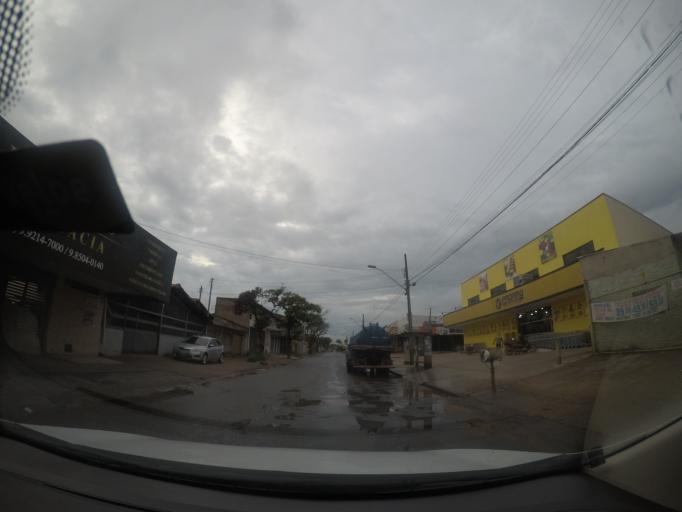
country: BR
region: Goias
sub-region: Goiania
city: Goiania
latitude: -16.6968
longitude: -49.3535
